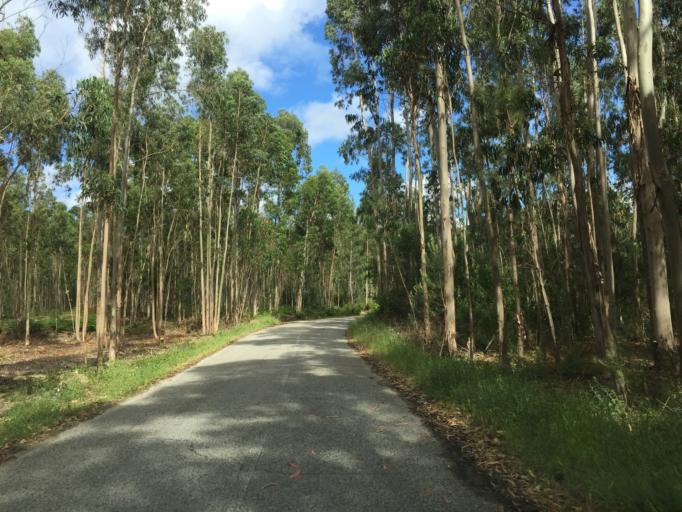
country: PT
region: Coimbra
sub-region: Figueira da Foz
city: Tavarede
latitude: 40.2112
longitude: -8.8356
